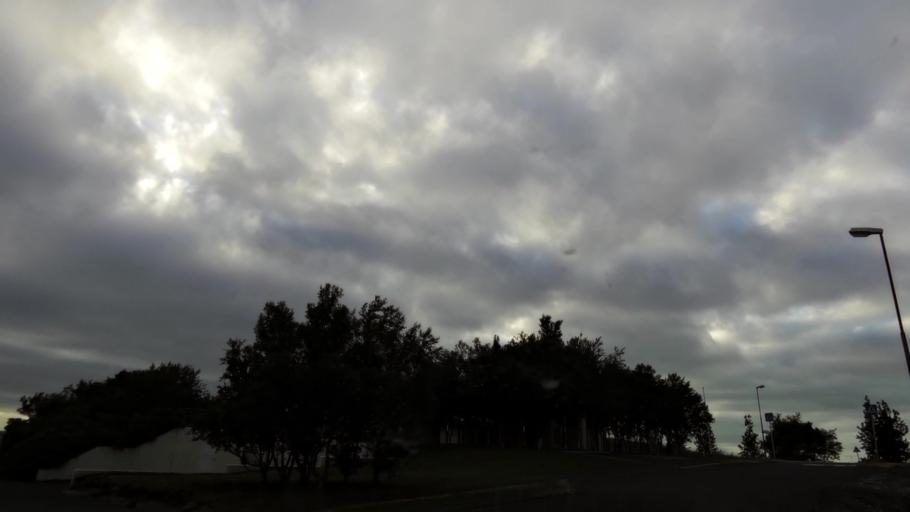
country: IS
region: Capital Region
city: Hafnarfjoerdur
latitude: 64.0607
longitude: -21.9540
